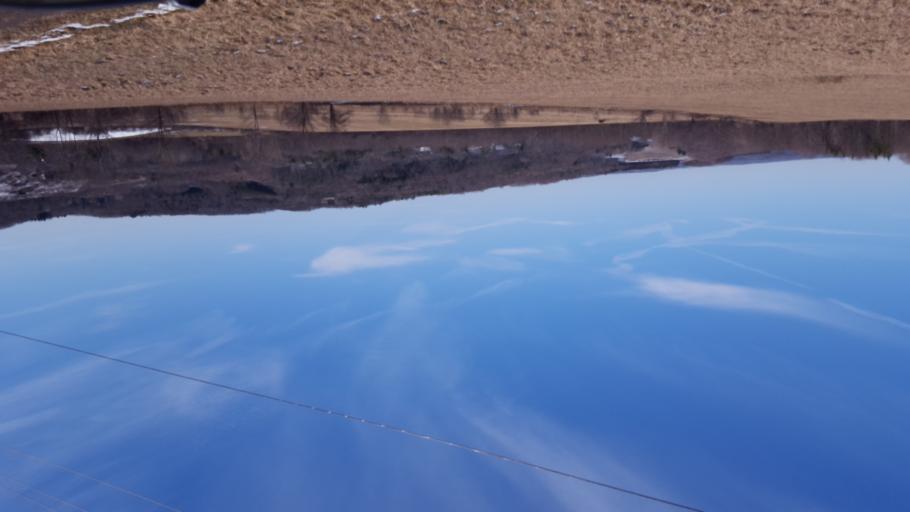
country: US
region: New York
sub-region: Allegany County
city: Wellsville
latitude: 42.0992
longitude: -77.9956
